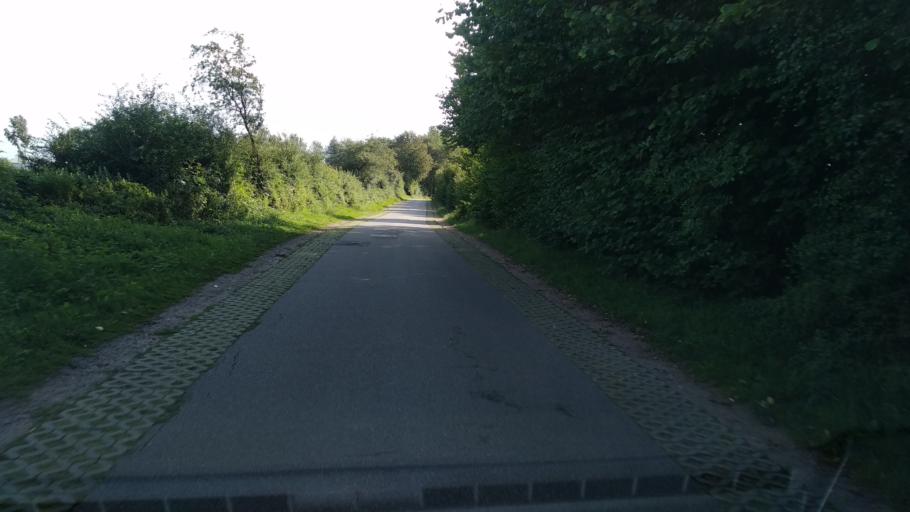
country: DE
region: Schleswig-Holstein
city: Busdorf
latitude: 54.4841
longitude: 9.5420
